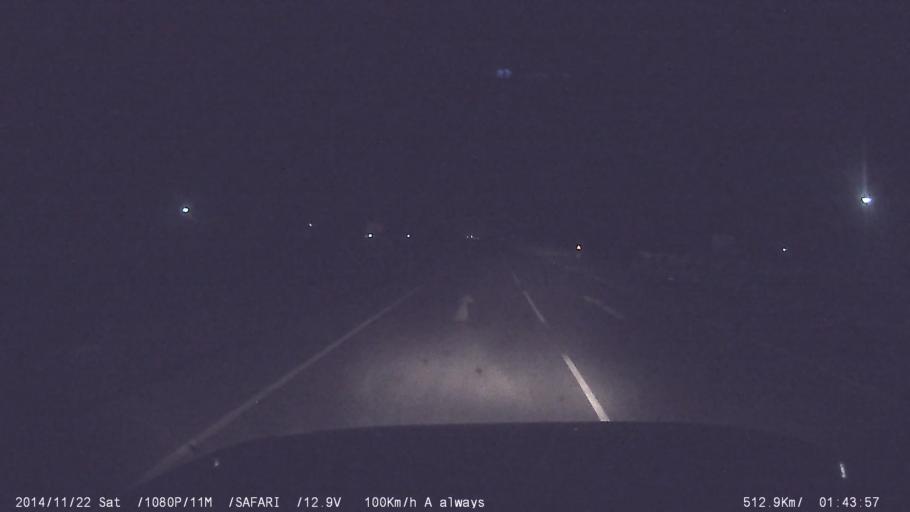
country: IN
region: Tamil Nadu
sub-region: Villupuram
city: Chinna Salem
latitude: 11.6736
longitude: 78.9127
